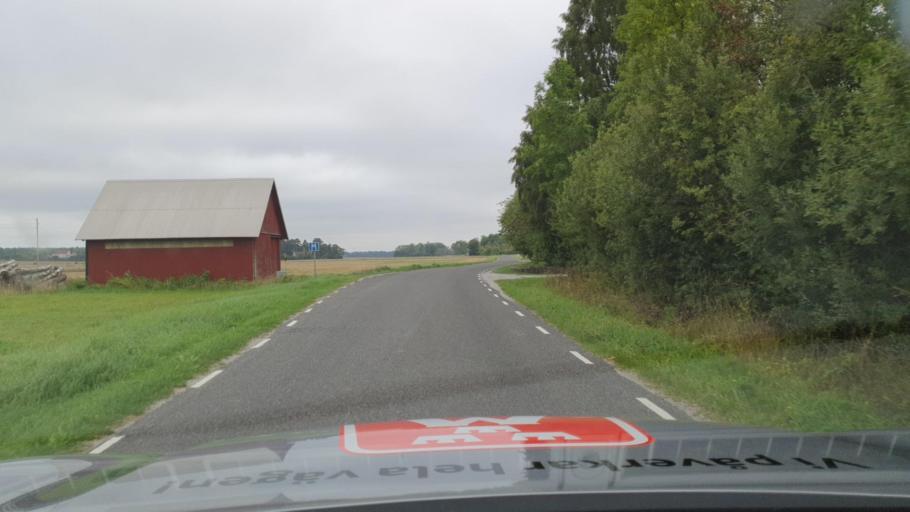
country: SE
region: Gotland
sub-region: Gotland
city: Visby
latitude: 57.6211
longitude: 18.4701
